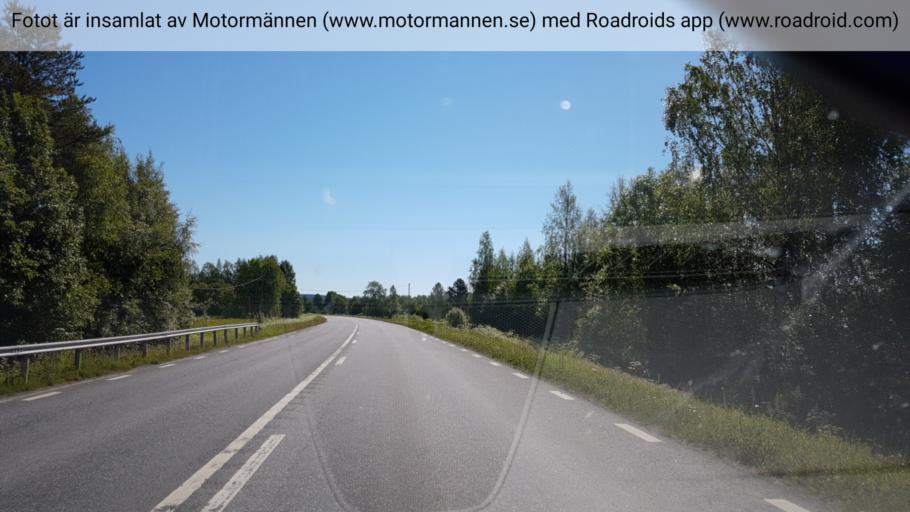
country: SE
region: Norrbotten
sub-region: Bodens Kommun
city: Boden
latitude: 65.8534
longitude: 21.4899
